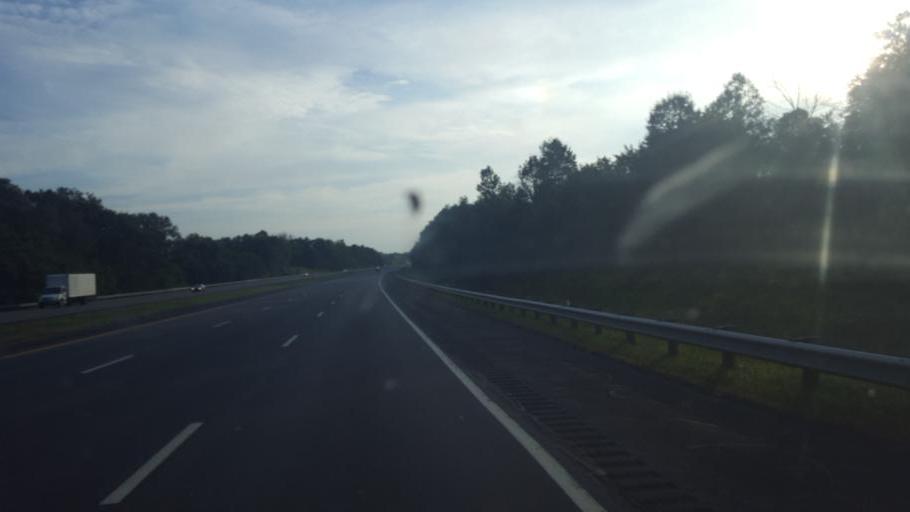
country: US
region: Ohio
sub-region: Richland County
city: Lexington
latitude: 40.5751
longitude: -82.6092
